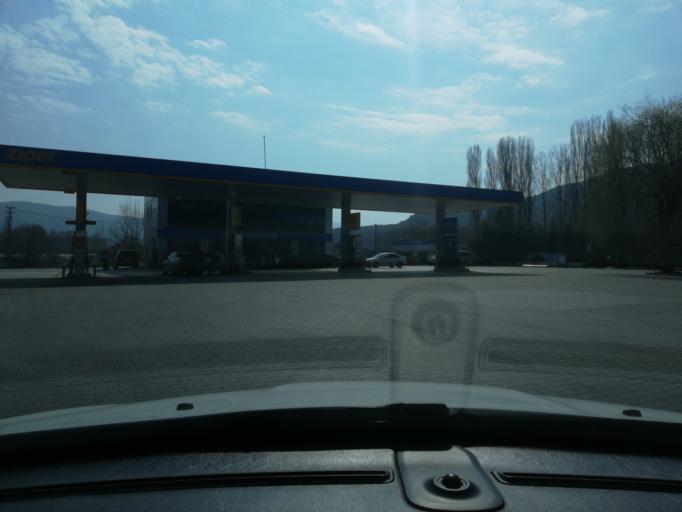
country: TR
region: Cankiri
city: Ilgaz
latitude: 40.9081
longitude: 33.6323
